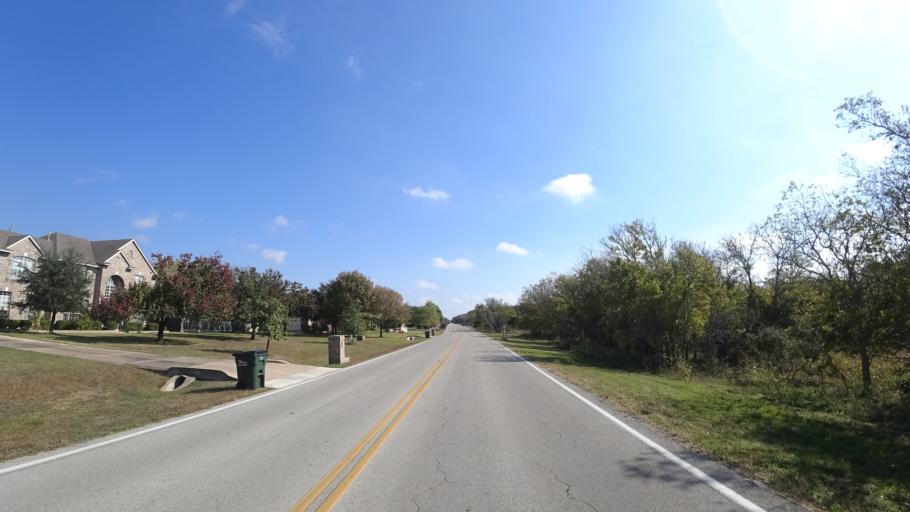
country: US
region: Texas
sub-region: Travis County
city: Shady Hollow
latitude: 30.1615
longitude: -97.8657
